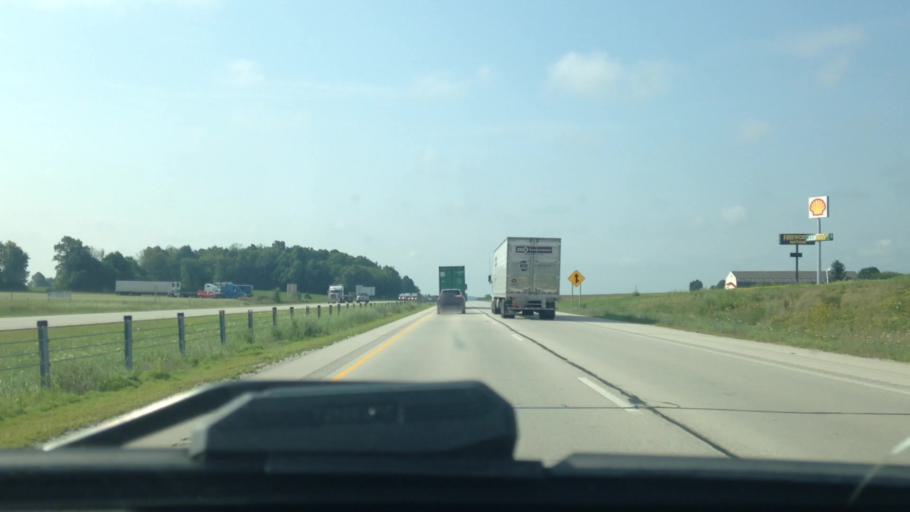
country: US
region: Wisconsin
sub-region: Dodge County
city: Lomira
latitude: 43.5861
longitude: -88.4308
